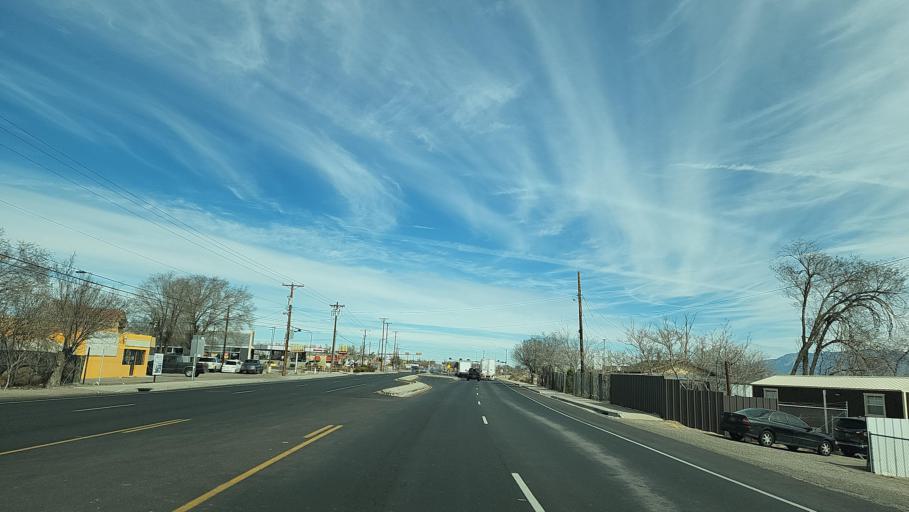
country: US
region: New Mexico
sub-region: Bernalillo County
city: South Valley
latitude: 35.0493
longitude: -106.7080
